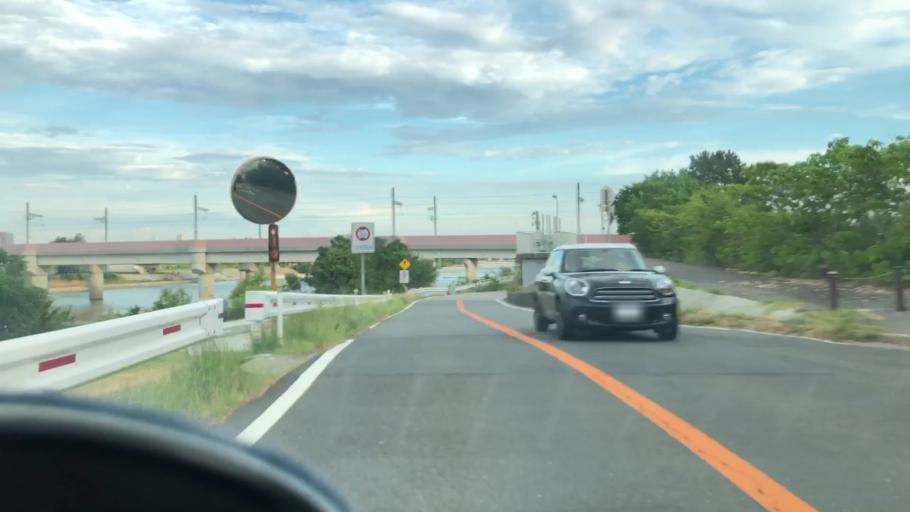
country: JP
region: Hyogo
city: Itami
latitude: 34.7500
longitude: 135.3741
